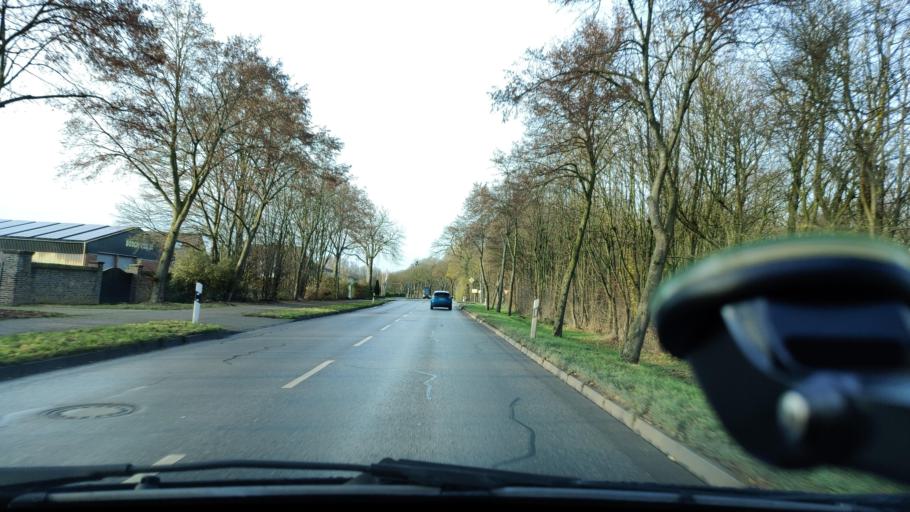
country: DE
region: North Rhine-Westphalia
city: Rees
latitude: 51.7254
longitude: 6.3520
